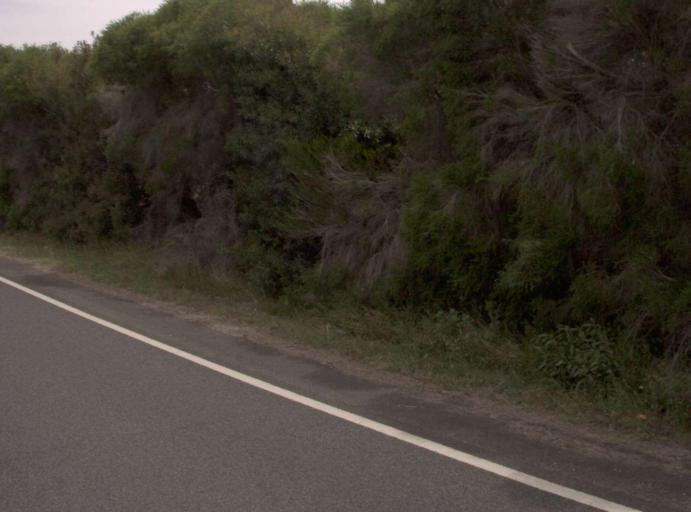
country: AU
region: Victoria
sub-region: Mornington Peninsula
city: Safety Beach
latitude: -38.3305
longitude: 144.9883
